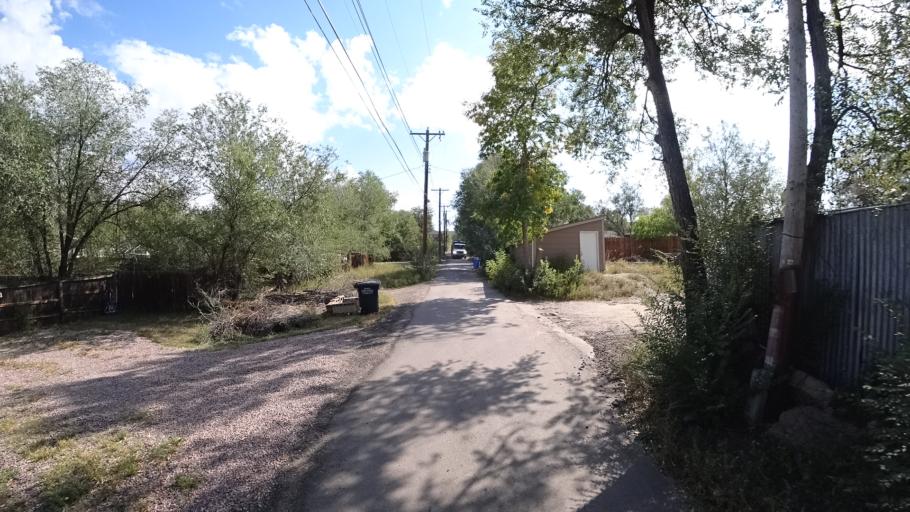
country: US
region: Colorado
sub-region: El Paso County
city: Colorado Springs
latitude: 38.8286
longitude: -104.8121
